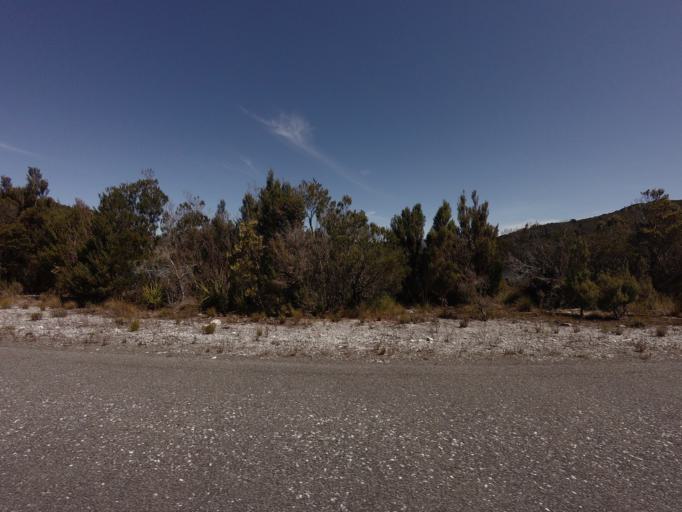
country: AU
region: Tasmania
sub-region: West Coast
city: Queenstown
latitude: -42.7962
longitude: 146.0704
